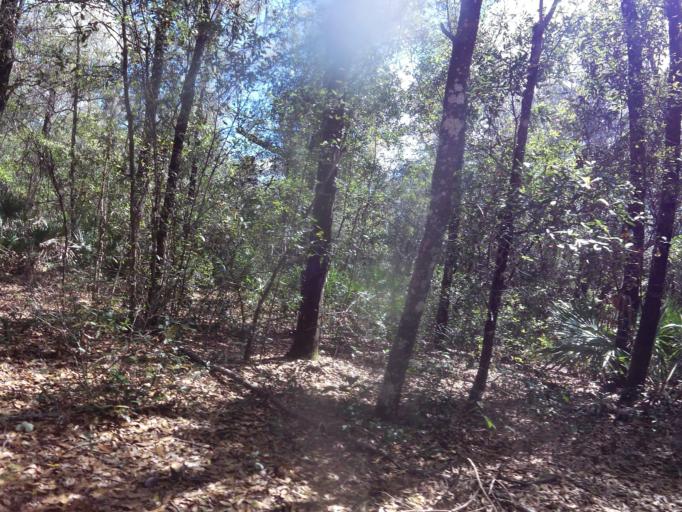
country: US
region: Florida
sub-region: Putnam County
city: Interlachen
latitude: 29.7649
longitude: -81.8632
